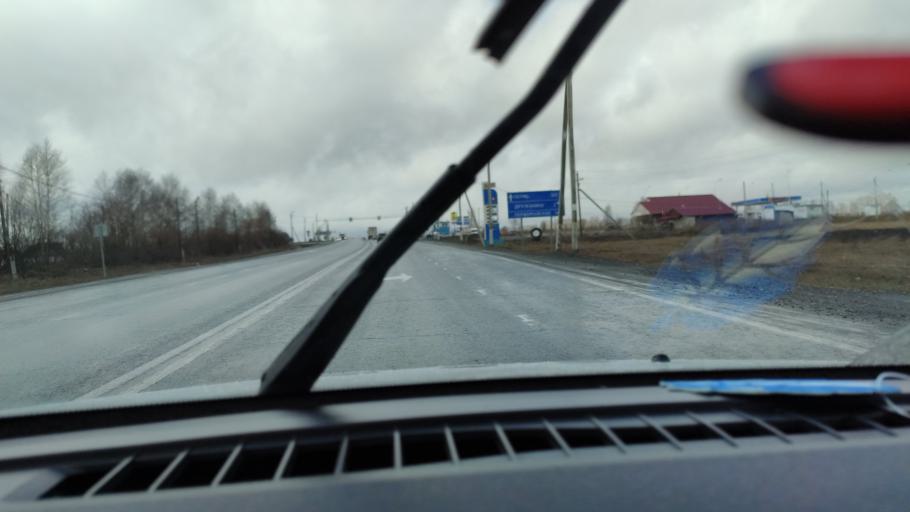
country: RU
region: Sverdlovsk
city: Druzhinino
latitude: 56.8107
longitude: 59.5293
